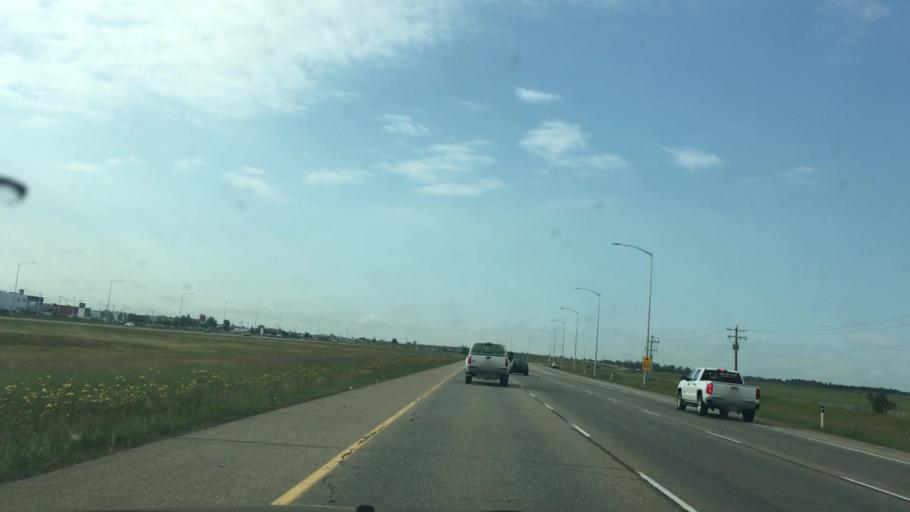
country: CA
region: Alberta
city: Leduc
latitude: 53.2941
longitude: -113.5497
